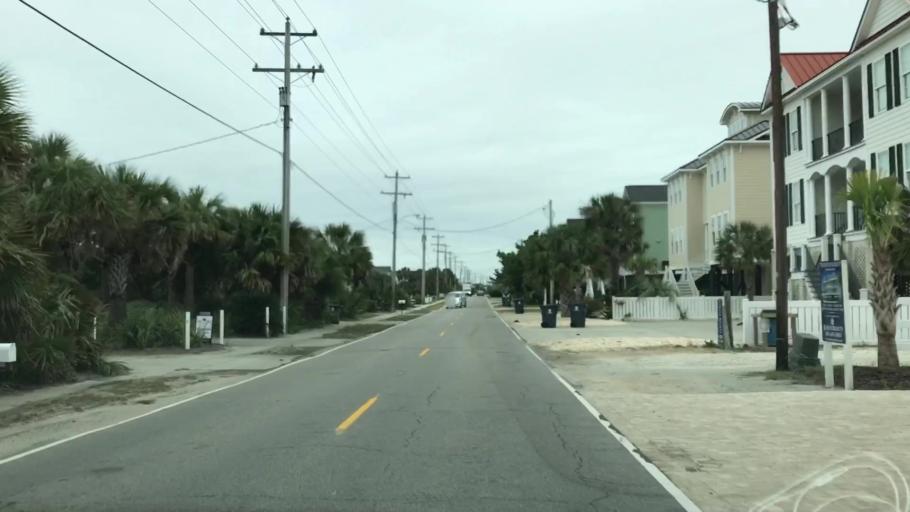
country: US
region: South Carolina
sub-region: Georgetown County
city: Murrells Inlet
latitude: 33.5604
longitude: -79.0128
